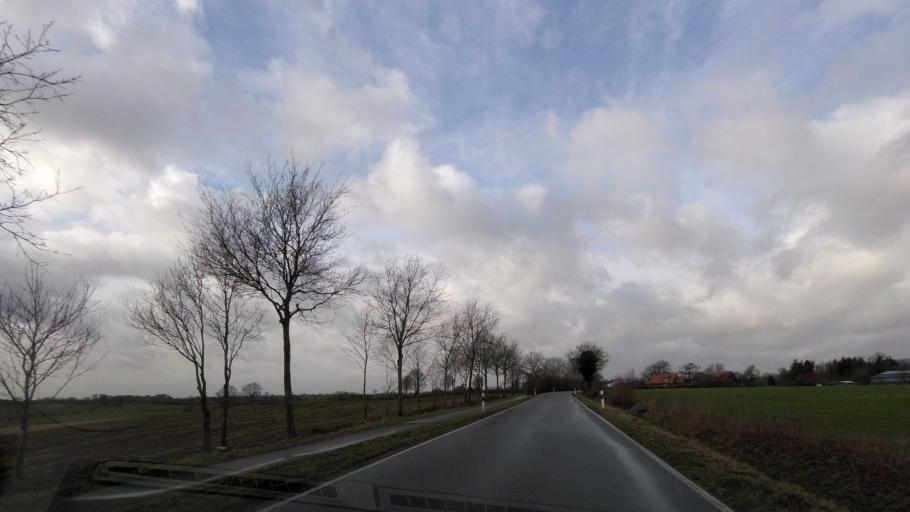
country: DE
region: Schleswig-Holstein
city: Rabenkirchen-Fauluck
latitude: 54.6329
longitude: 9.8803
